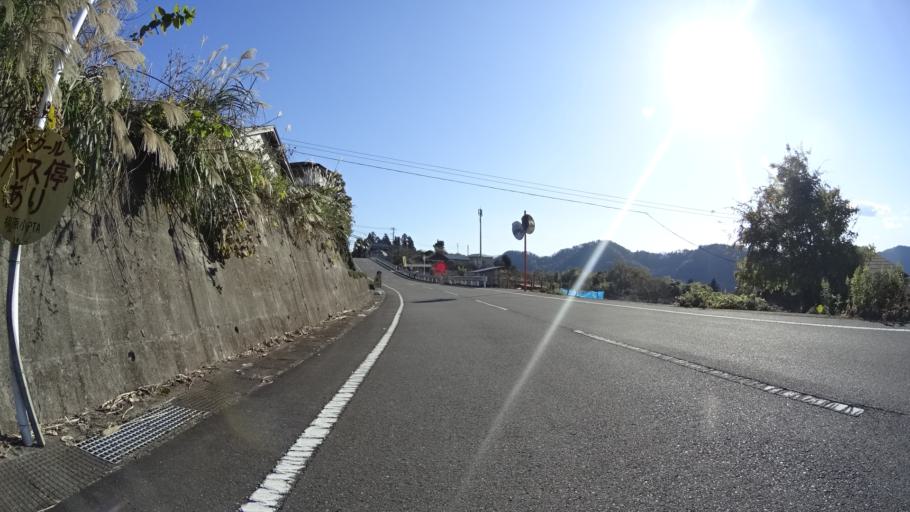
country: JP
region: Yamanashi
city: Uenohara
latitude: 35.6641
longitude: 139.1158
